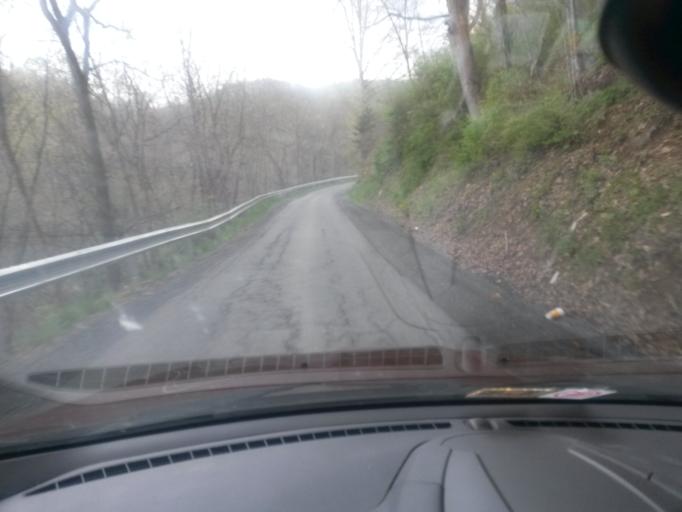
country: US
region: West Virginia
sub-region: Greenbrier County
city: Lewisburg
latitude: 37.9373
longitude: -80.4225
